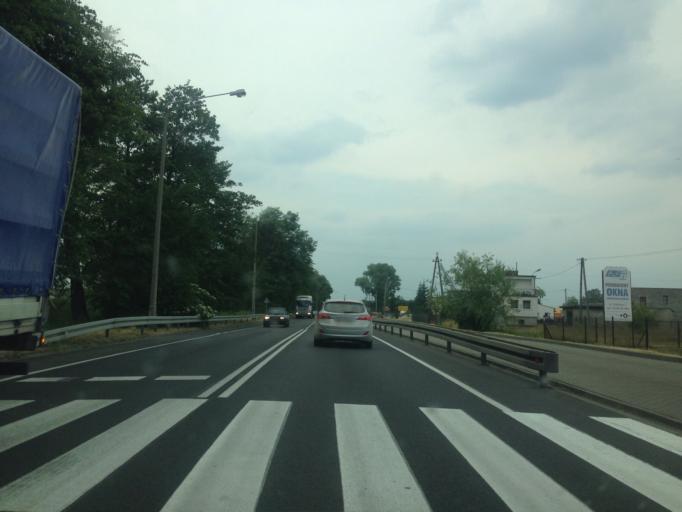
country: PL
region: Kujawsko-Pomorskie
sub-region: Grudziadz
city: Grudziadz
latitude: 53.5029
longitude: 18.8430
